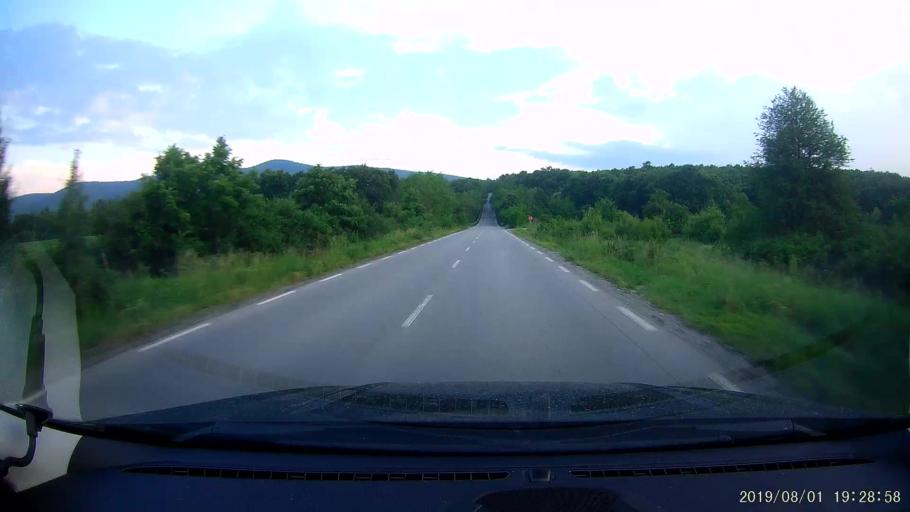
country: BG
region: Burgas
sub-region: Obshtina Sungurlare
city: Sungurlare
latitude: 42.8339
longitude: 26.9118
